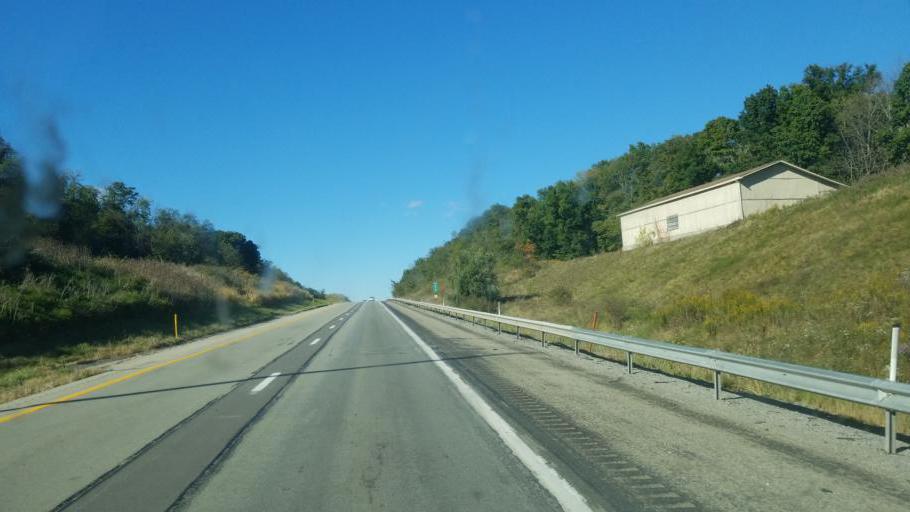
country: US
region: Pennsylvania
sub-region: Washington County
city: East Washington
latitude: 40.0855
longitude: -80.1927
